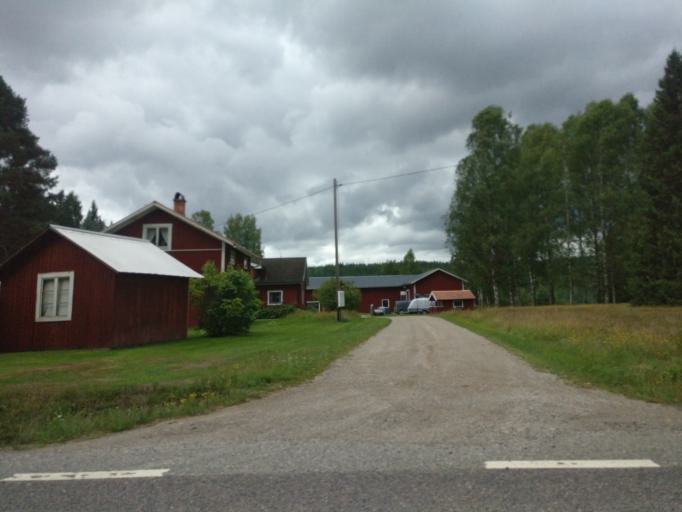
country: SE
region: Vaermland
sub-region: Torsby Kommun
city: Torsby
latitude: 60.7660
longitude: 12.7596
